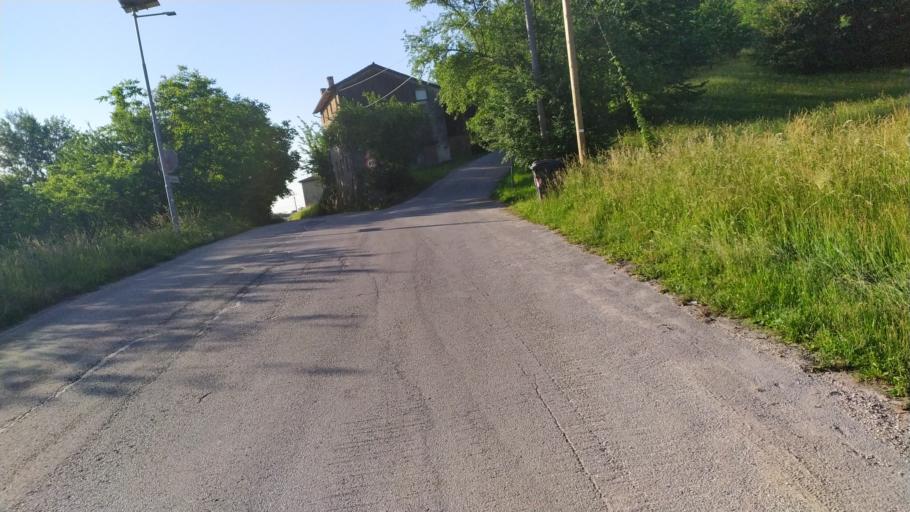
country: IT
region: Veneto
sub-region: Provincia di Vicenza
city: Malo
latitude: 45.6461
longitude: 11.4183
